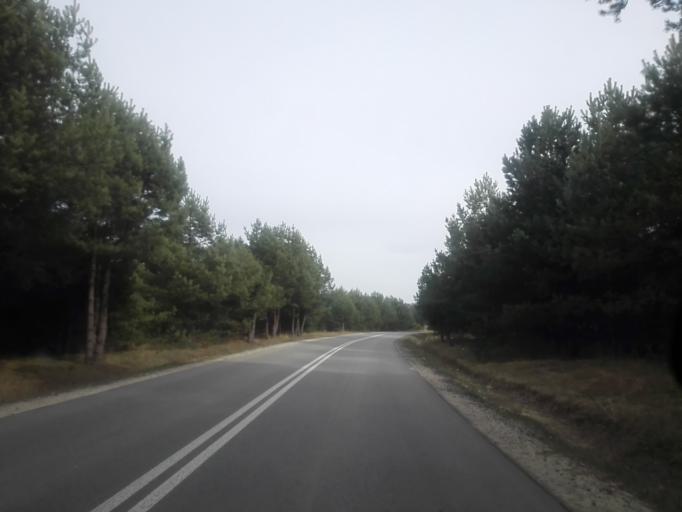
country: PL
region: Silesian Voivodeship
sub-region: Powiat czestochowski
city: Potok Zloty
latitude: 50.7058
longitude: 19.3549
